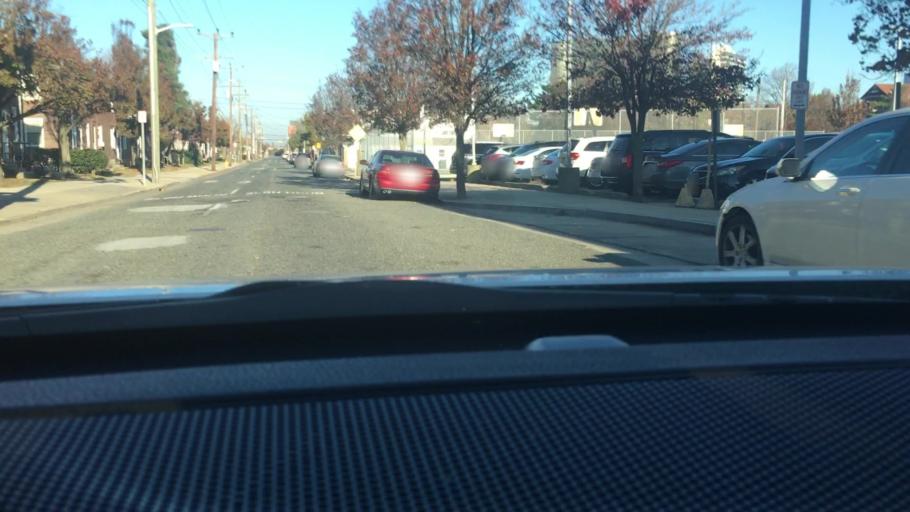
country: US
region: New Jersey
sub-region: Atlantic County
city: Atlantic City
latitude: 39.3677
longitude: -74.4334
